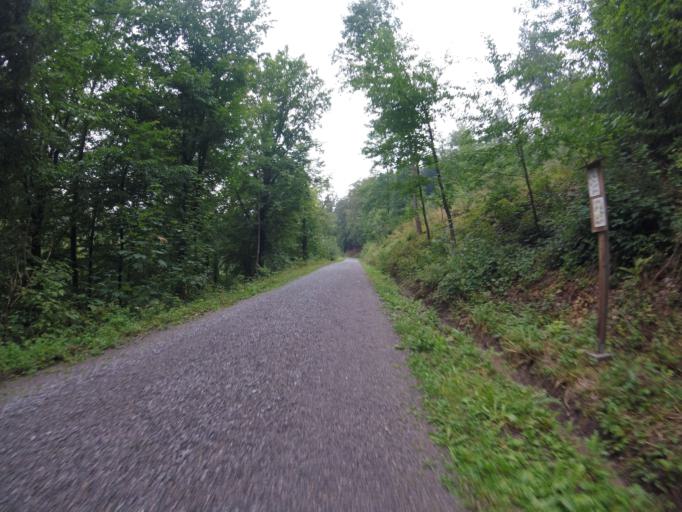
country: DE
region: Baden-Wuerttemberg
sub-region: Regierungsbezirk Stuttgart
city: Oppenweiler
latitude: 48.9851
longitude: 9.4320
